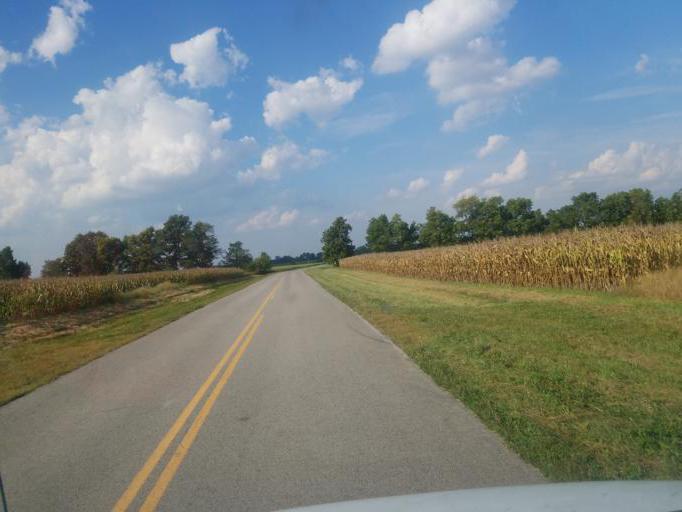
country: US
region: Ohio
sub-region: Hancock County
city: Arlington
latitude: 40.8863
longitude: -83.5683
